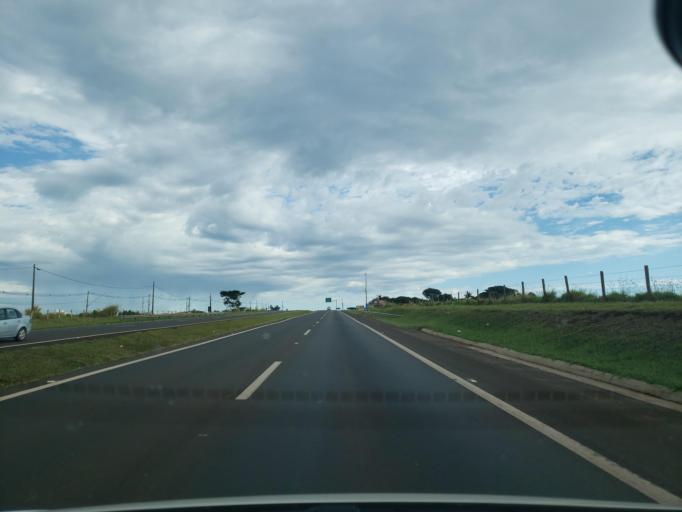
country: BR
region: Sao Paulo
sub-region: Jau
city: Jau
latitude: -22.2588
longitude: -48.5433
